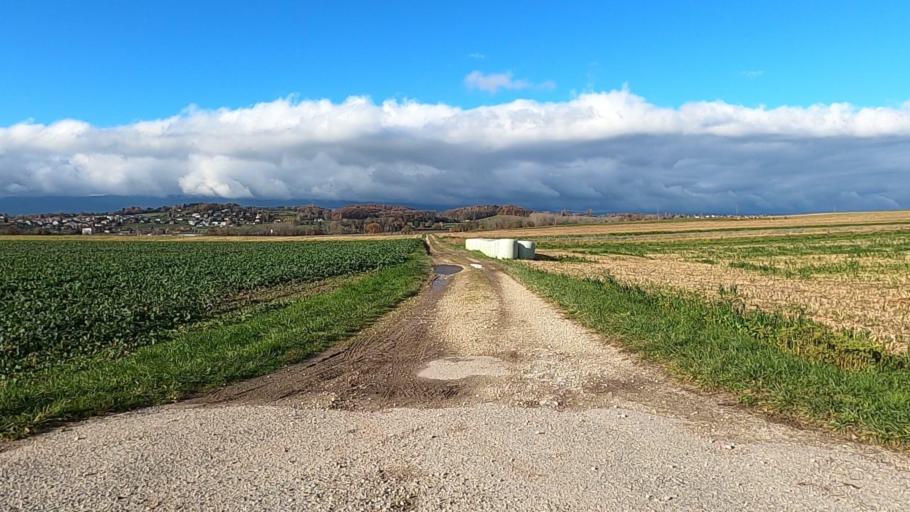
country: CH
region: Vaud
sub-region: Morges District
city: Saint-Prex
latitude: 46.5141
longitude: 6.4448
